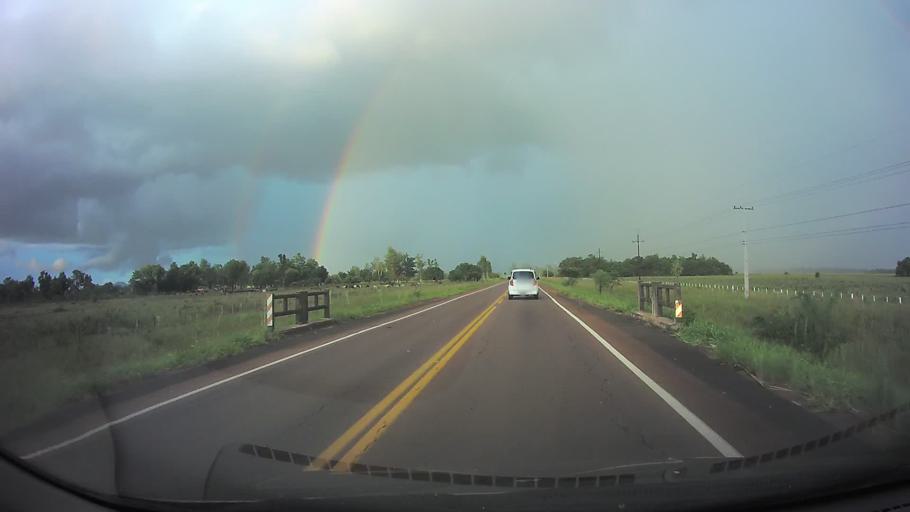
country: PY
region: Paraguari
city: Carapegua
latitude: -25.7124
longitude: -57.1916
